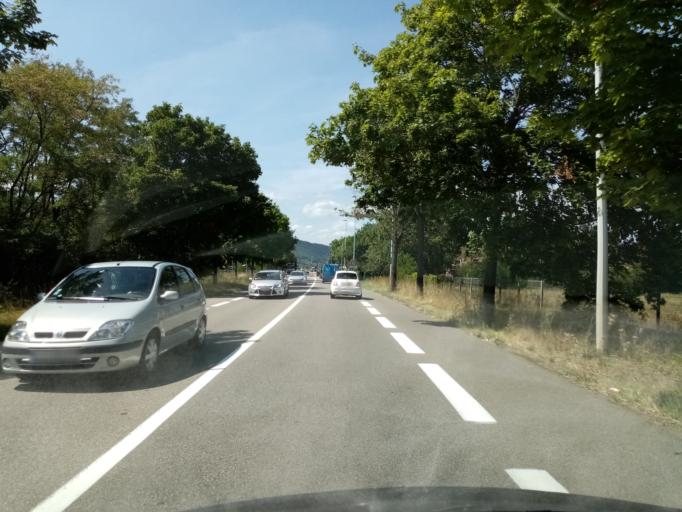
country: FR
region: Alsace
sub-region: Departement du Bas-Rhin
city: Selestat
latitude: 48.2529
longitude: 7.4304
